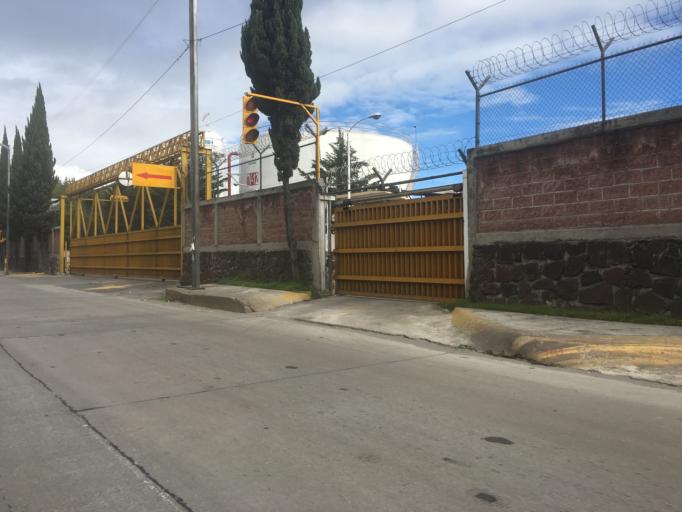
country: MX
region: Mexico
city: Santa Maria Totoltepec
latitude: 19.2880
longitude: -99.6026
